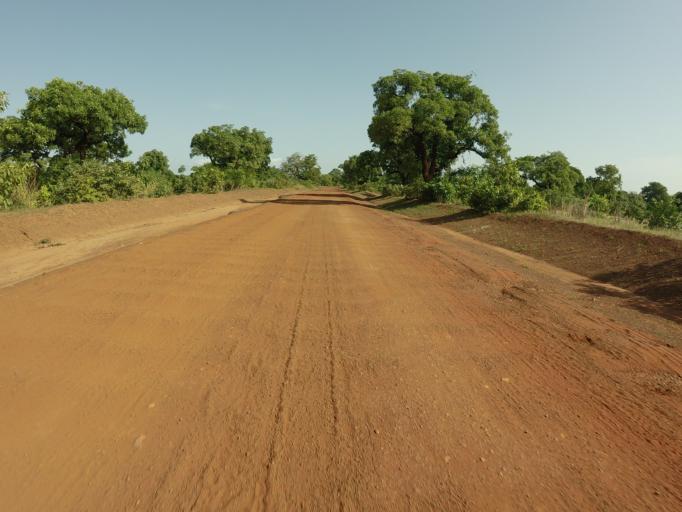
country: GH
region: Upper East
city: Bawku
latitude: 10.7421
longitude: -0.2004
